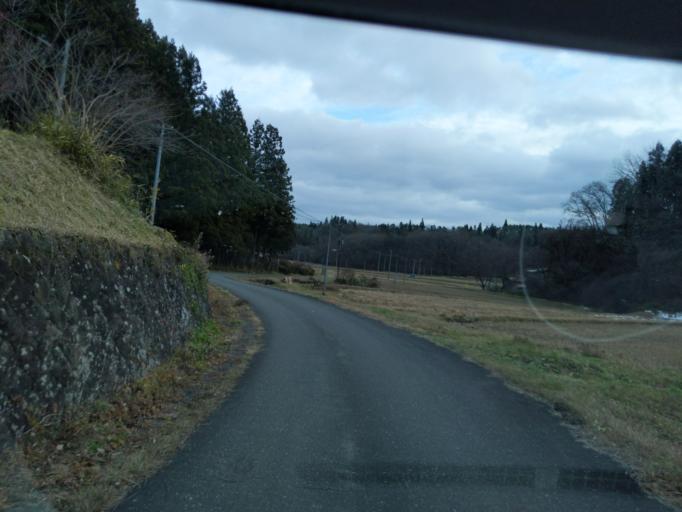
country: JP
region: Iwate
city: Ichinoseki
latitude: 38.9710
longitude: 141.0593
